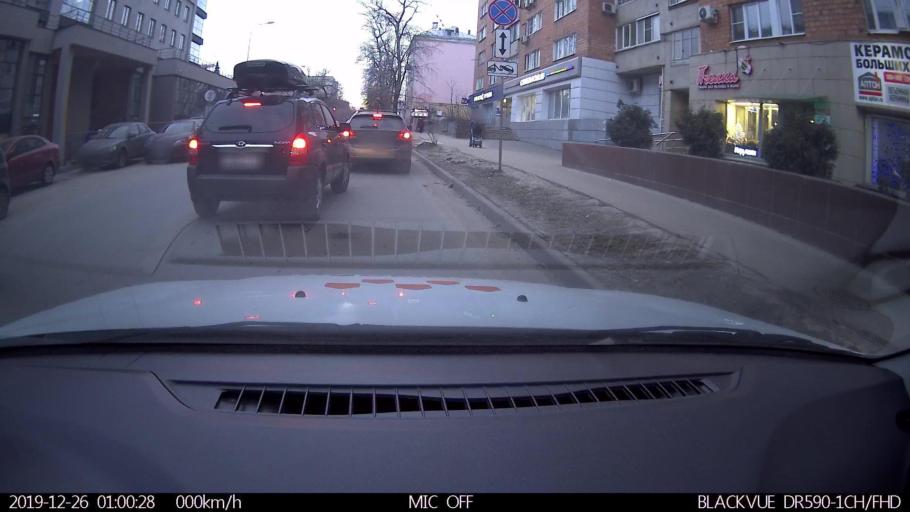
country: RU
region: Nizjnij Novgorod
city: Nizhniy Novgorod
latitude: 56.3182
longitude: 44.0106
